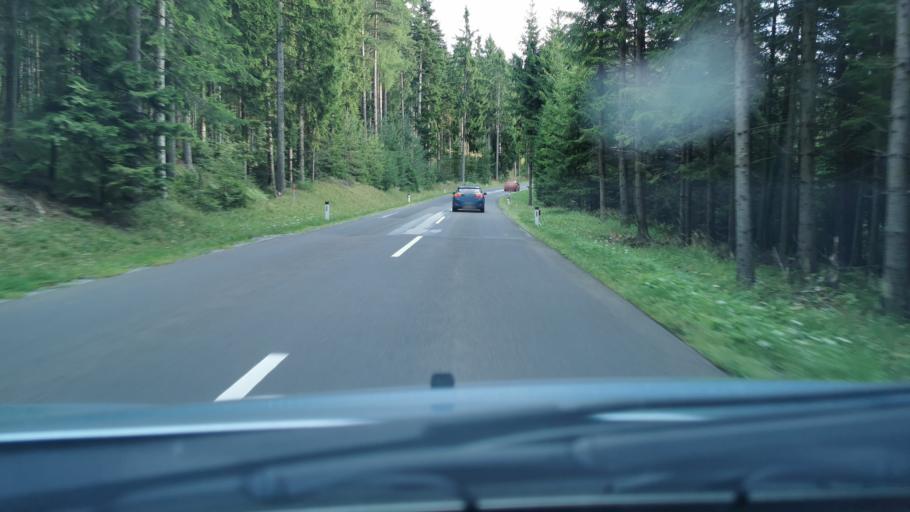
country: AT
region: Styria
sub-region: Politischer Bezirk Weiz
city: Fischbach
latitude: 47.4148
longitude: 15.6584
